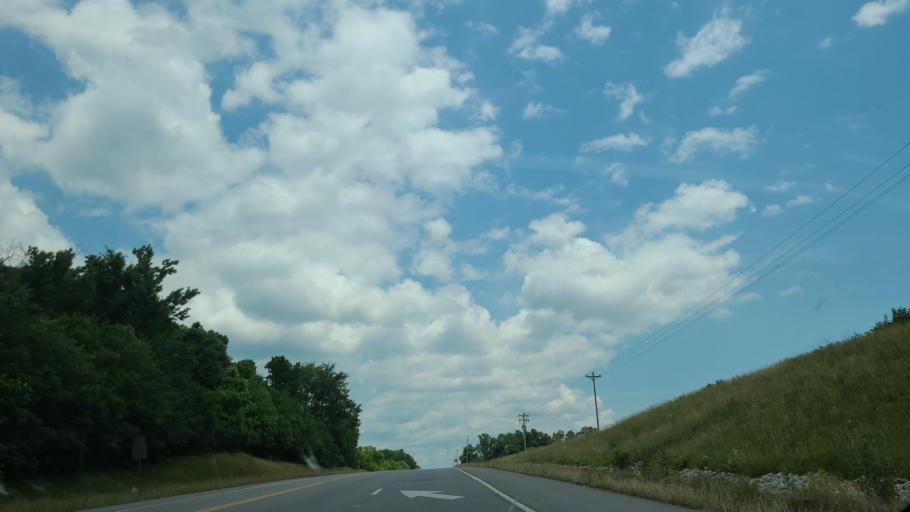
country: US
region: Tennessee
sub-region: Bledsoe County
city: Pikeville
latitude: 35.6197
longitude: -85.1843
